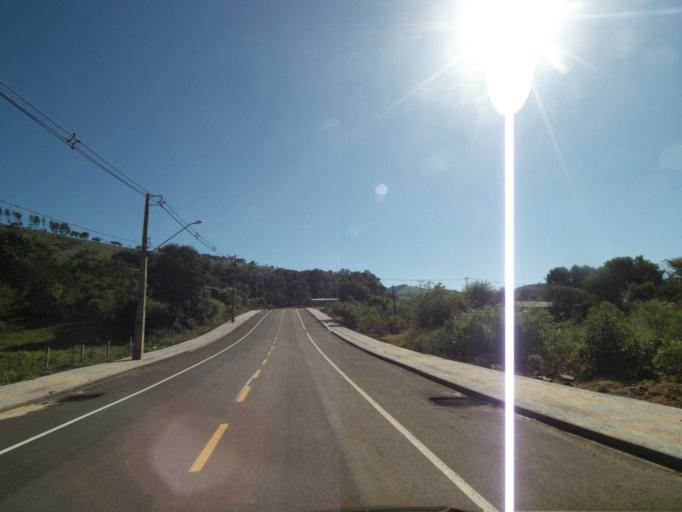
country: BR
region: Parana
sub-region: Francisco Beltrao
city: Francisco Beltrao
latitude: -26.1428
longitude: -53.3154
